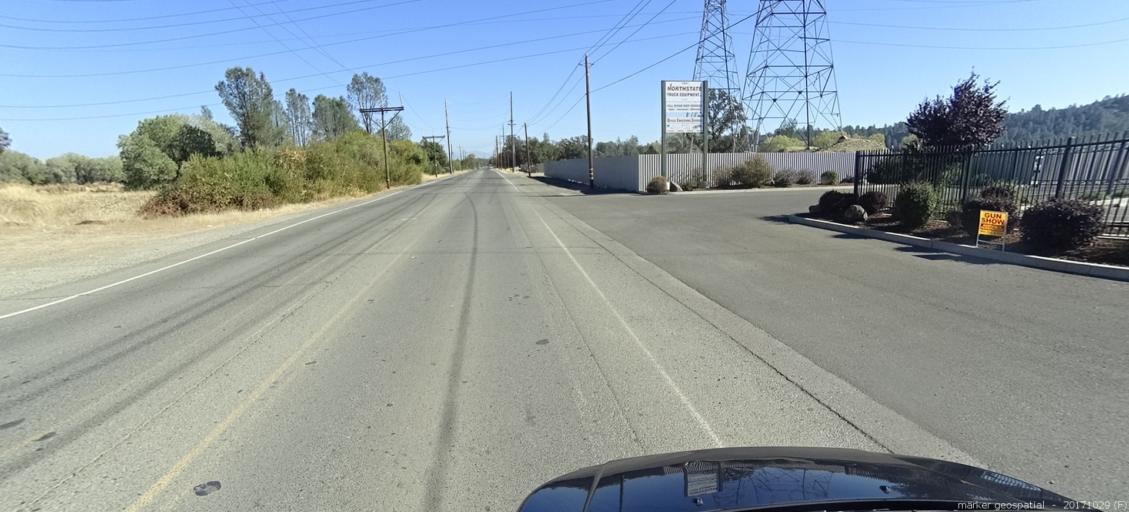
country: US
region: California
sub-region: Shasta County
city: Redding
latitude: 40.5026
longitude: -122.4275
